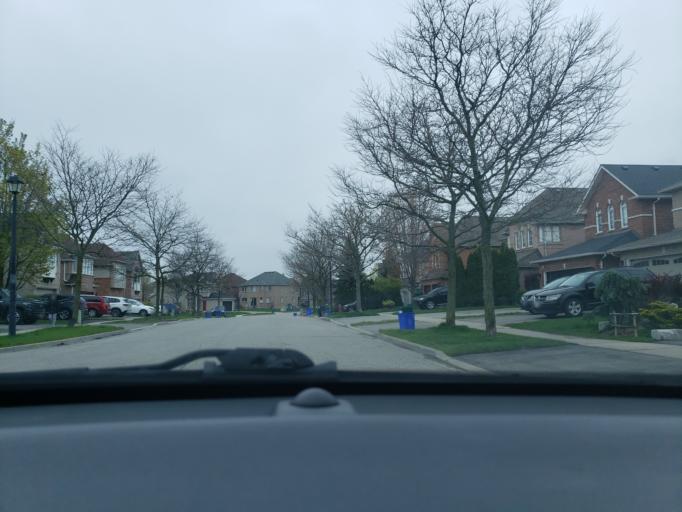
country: CA
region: Ontario
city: Newmarket
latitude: 44.0347
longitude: -79.4554
